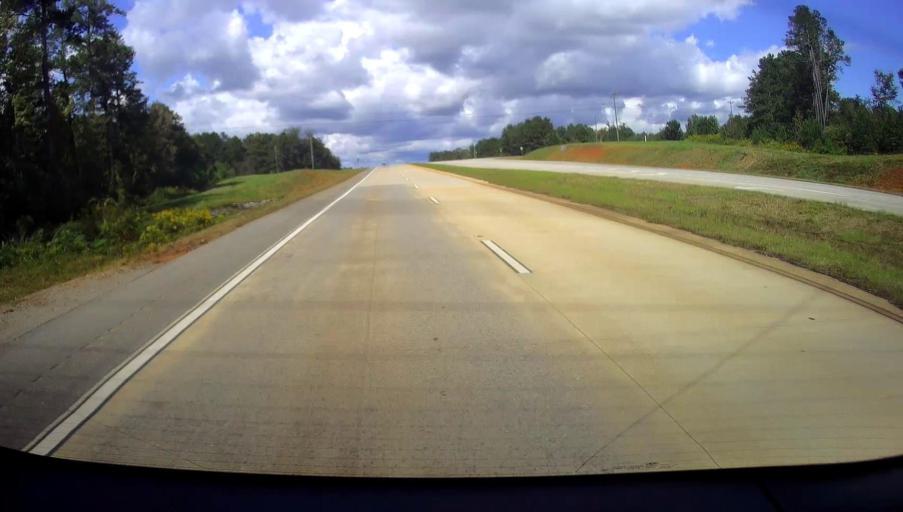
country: US
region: Georgia
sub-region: Jones County
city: Gray
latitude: 32.9953
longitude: -83.5742
